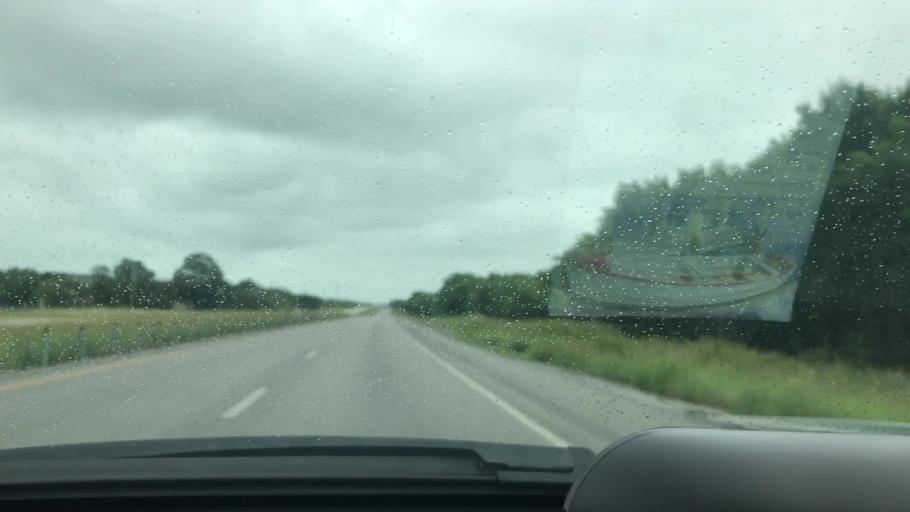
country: US
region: Oklahoma
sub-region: Coal County
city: Coalgate
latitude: 34.6147
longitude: -95.9691
